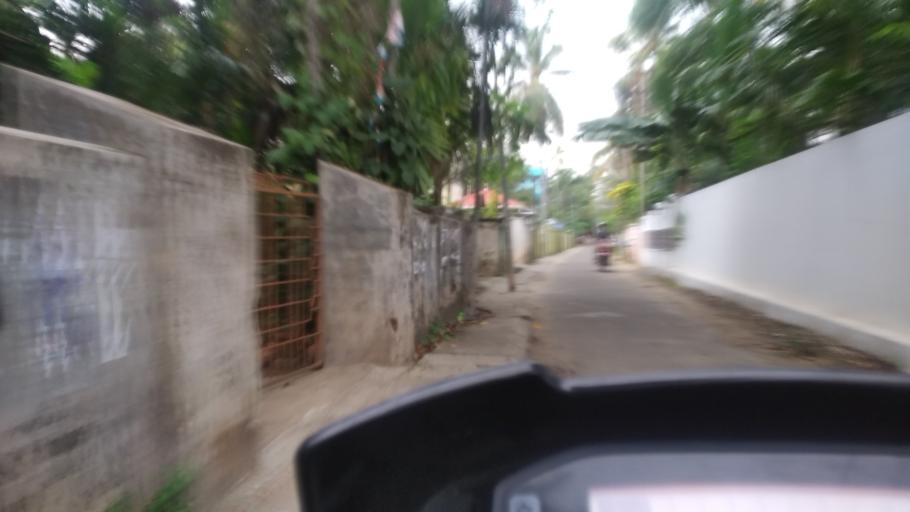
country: IN
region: Kerala
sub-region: Ernakulam
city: Elur
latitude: 10.0640
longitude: 76.2159
